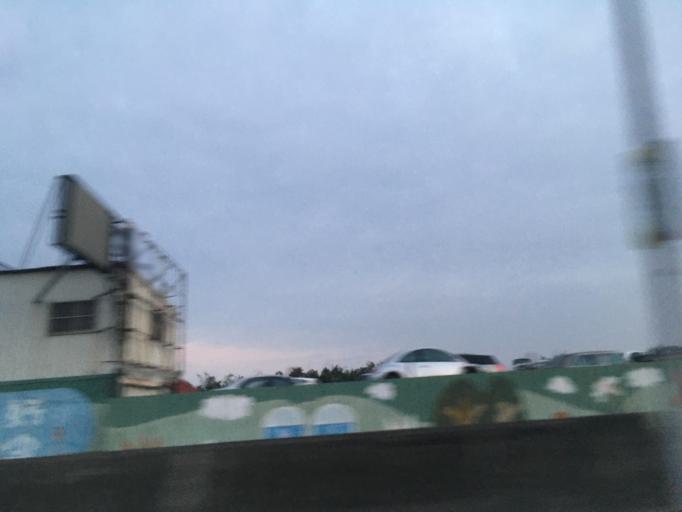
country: TW
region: Taiwan
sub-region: Chiayi
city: Jiayi Shi
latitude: 23.5836
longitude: 120.4625
